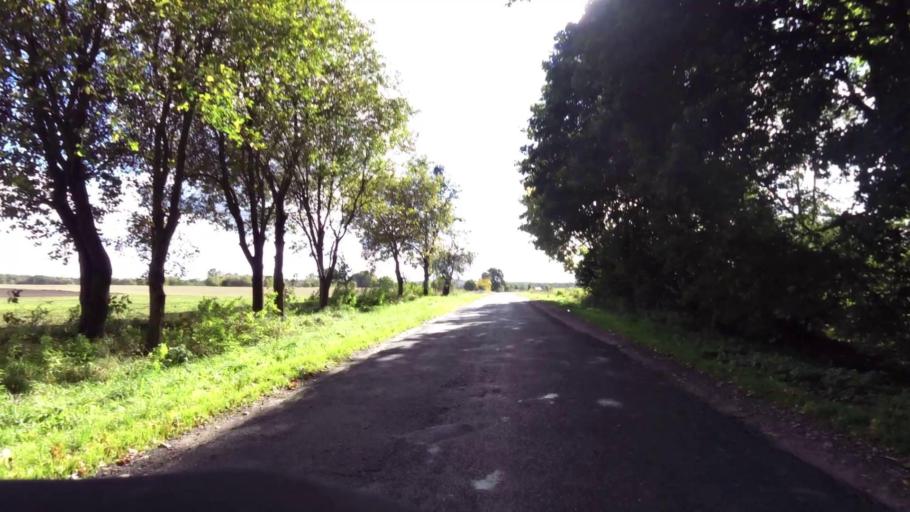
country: PL
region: West Pomeranian Voivodeship
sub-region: Powiat bialogardzki
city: Bialogard
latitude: 53.9955
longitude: 16.0633
